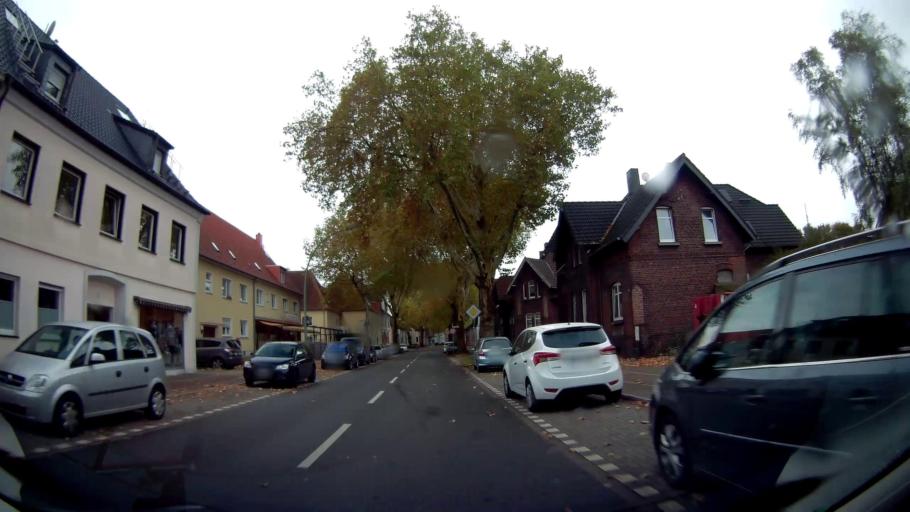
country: DE
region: North Rhine-Westphalia
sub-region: Regierungsbezirk Munster
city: Bottrop
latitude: 51.5358
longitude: 6.9538
